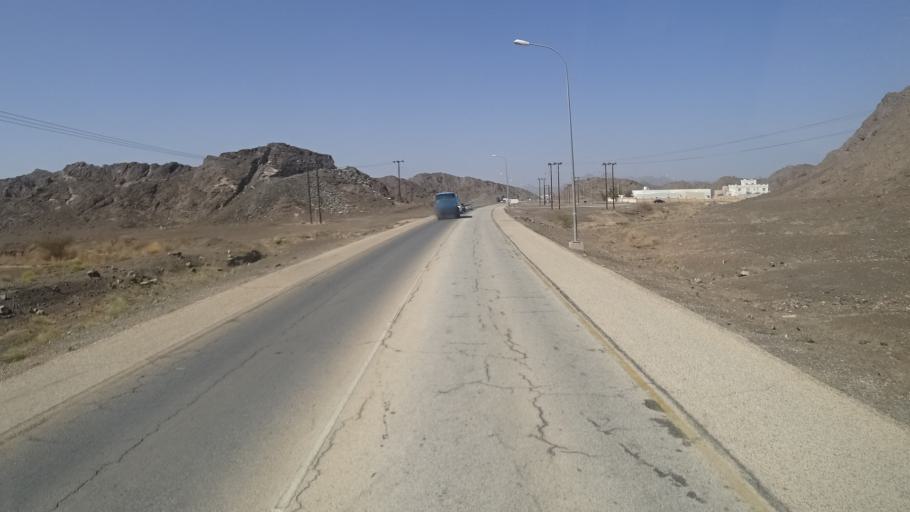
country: OM
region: Ash Sharqiyah
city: Ibra'
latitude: 22.6841
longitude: 58.5687
